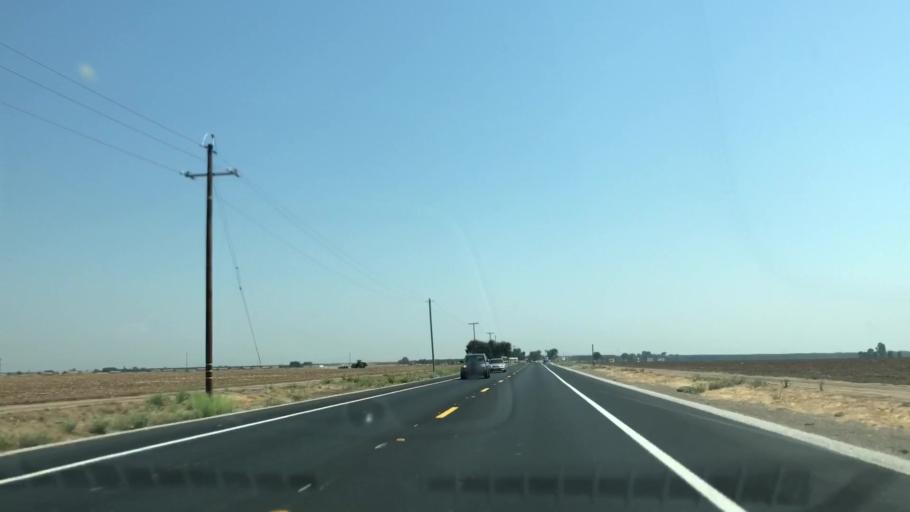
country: US
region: California
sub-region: San Joaquin County
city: Linden
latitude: 37.9422
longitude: -121.1191
